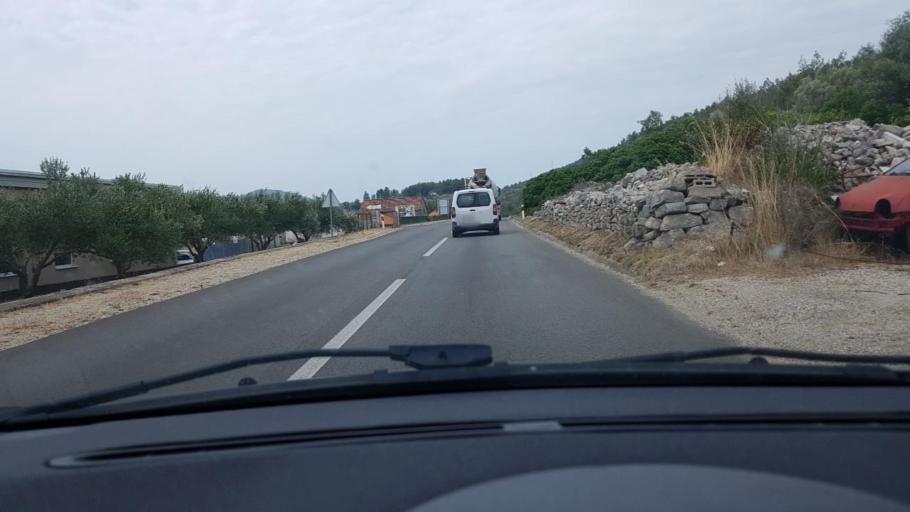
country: HR
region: Dubrovacko-Neretvanska
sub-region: Grad Dubrovnik
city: Vela Luka
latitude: 42.9476
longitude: 16.7745
